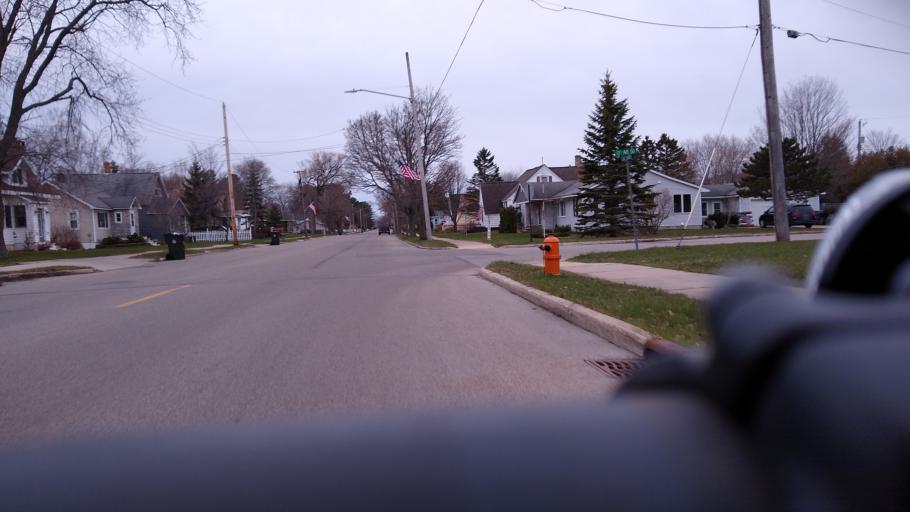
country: US
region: Michigan
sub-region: Delta County
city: Escanaba
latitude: 45.7312
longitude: -87.0637
